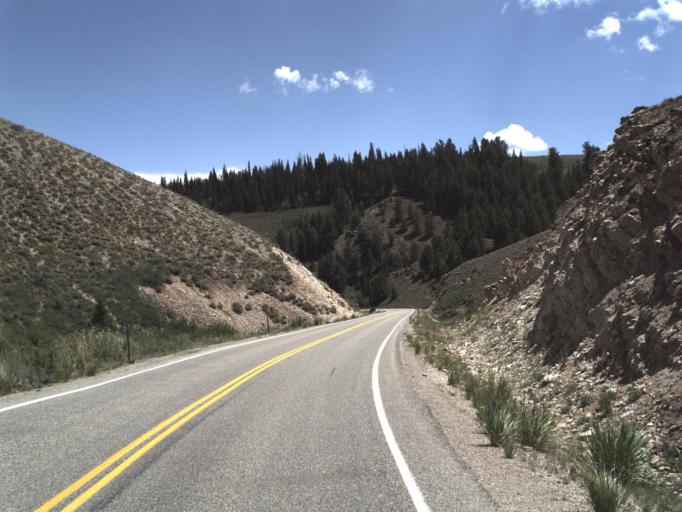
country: US
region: Utah
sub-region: Rich County
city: Randolph
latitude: 41.4848
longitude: -111.3946
